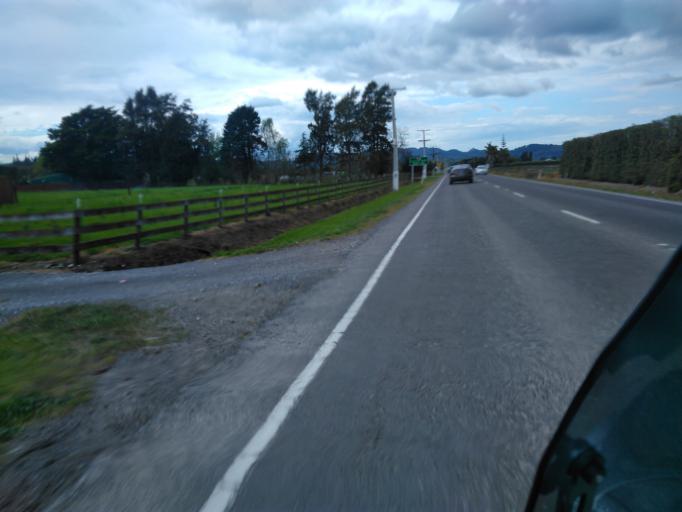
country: NZ
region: Gisborne
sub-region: Gisborne District
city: Gisborne
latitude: -38.6559
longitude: 177.9508
